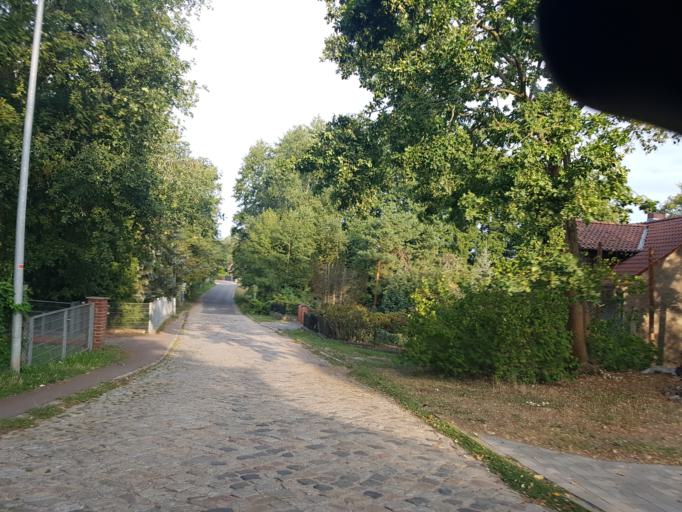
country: DE
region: Saxony-Anhalt
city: Coswig
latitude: 51.8873
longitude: 12.4686
